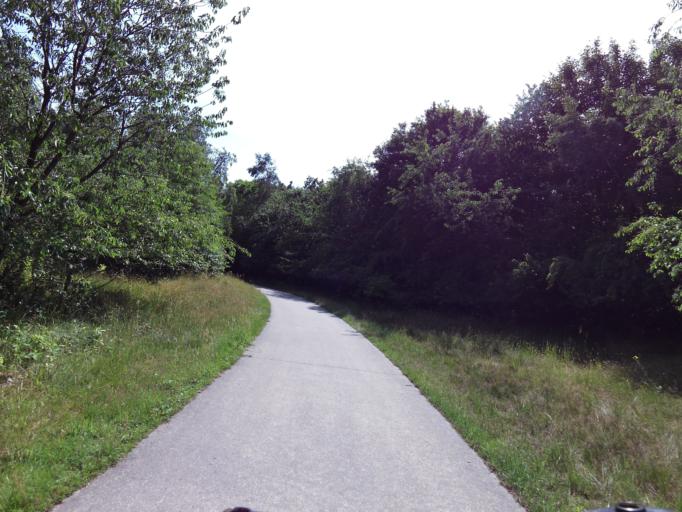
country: NL
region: Zeeland
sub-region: Schouwen-Duiveland
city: Burgh
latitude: 51.6862
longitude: 3.7084
